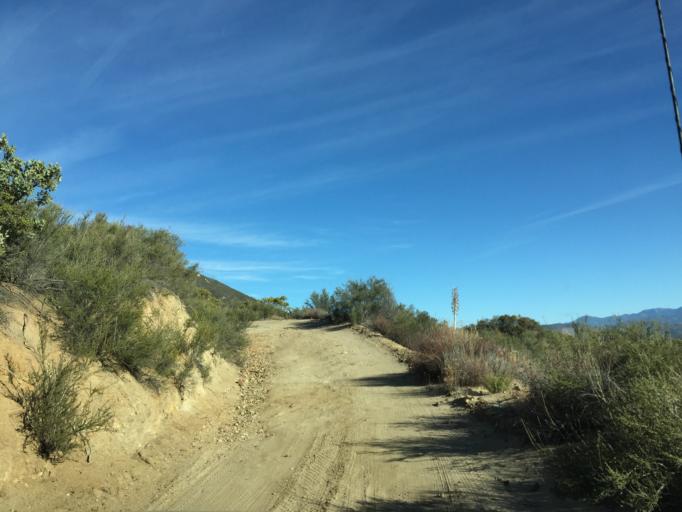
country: US
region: California
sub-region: Riverside County
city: Anza
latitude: 33.5924
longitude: -116.7728
